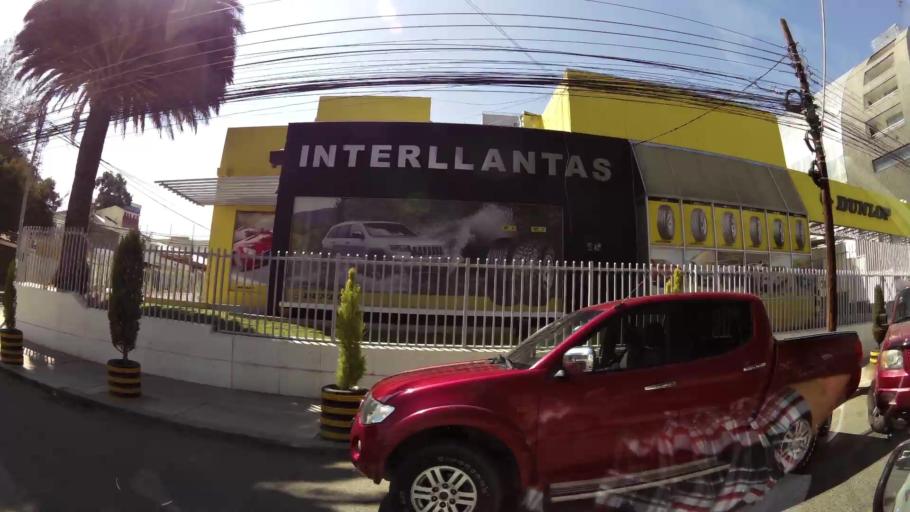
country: BO
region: La Paz
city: La Paz
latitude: -16.5400
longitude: -68.0829
